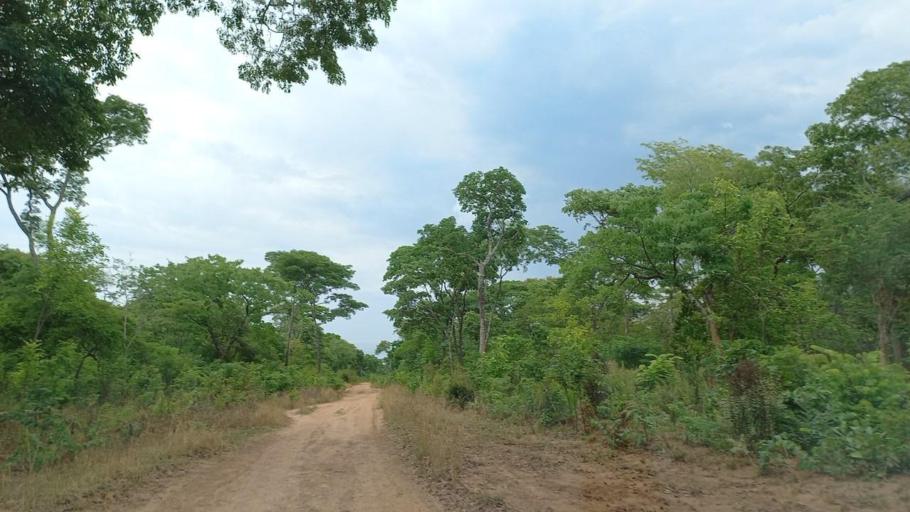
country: ZM
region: North-Western
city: Kalengwa
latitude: -13.5343
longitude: 24.9797
